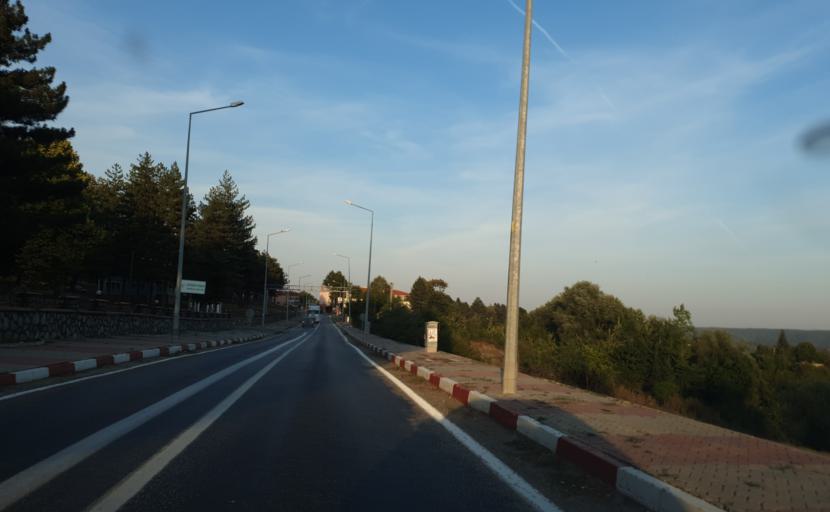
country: TR
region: Kirklareli
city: Sergen
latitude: 41.8216
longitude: 27.7588
